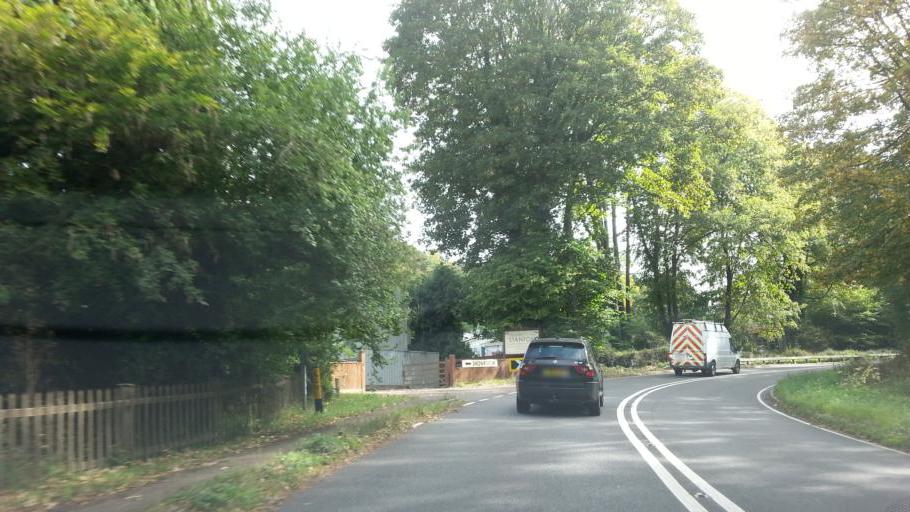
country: GB
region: England
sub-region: Gloucestershire
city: Mitcheldean
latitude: 51.8799
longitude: -2.4566
